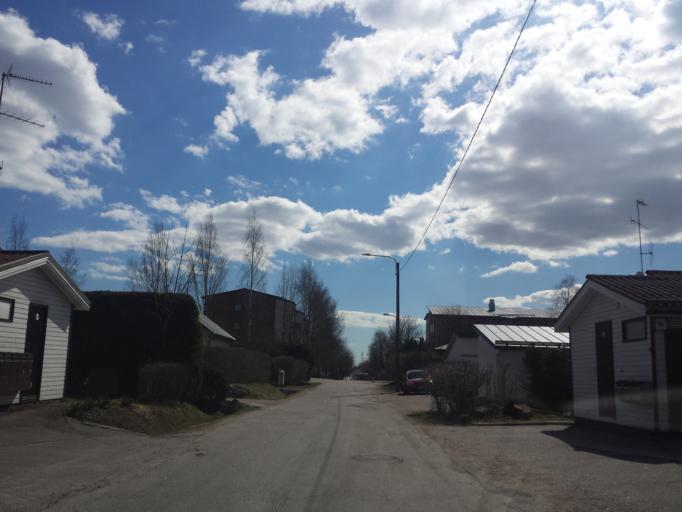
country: FI
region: Uusimaa
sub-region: Helsinki
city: Vantaa
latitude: 60.2954
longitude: 25.0232
